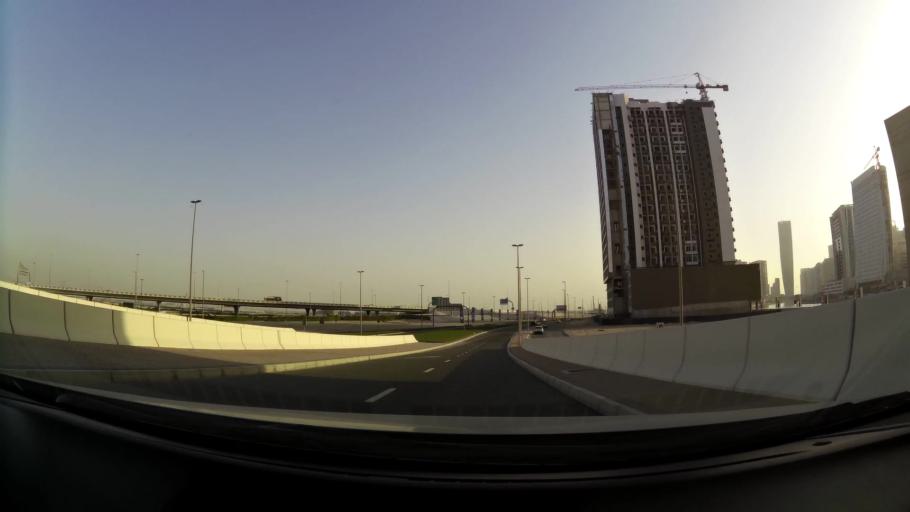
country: AE
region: Dubai
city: Dubai
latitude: 25.1849
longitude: 55.2859
